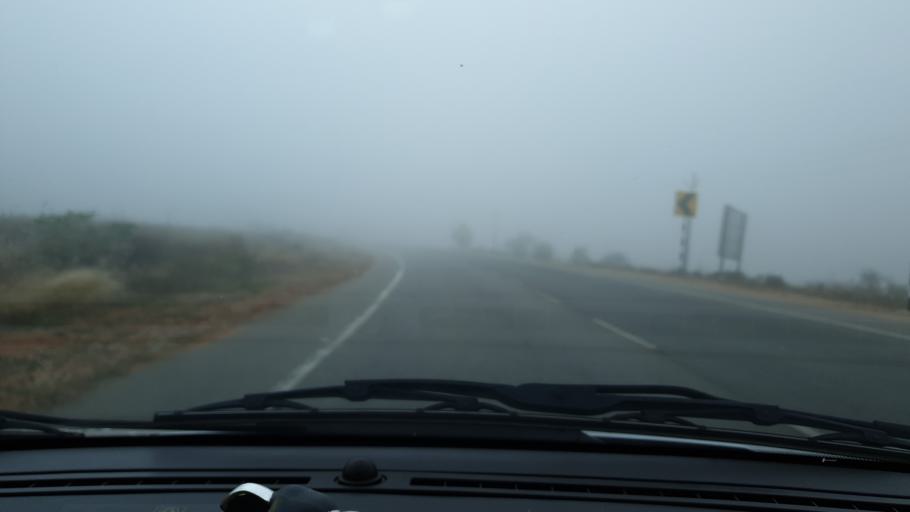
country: IN
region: Telangana
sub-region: Mahbubnagar
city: Nagar Karnul
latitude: 16.6661
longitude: 78.5300
